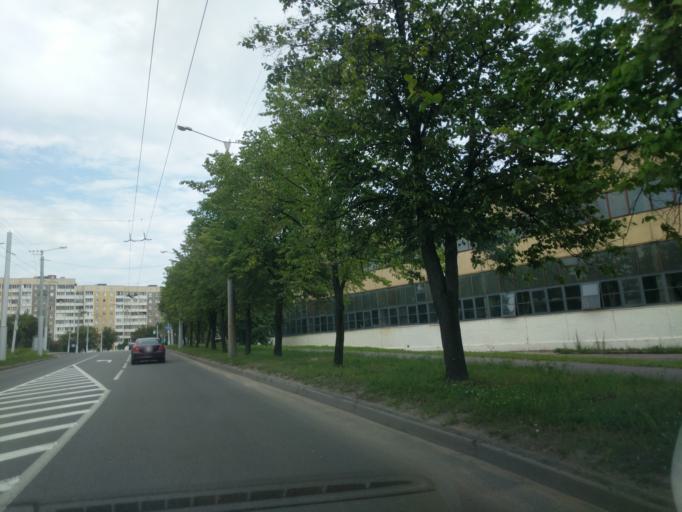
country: BY
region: Minsk
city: Novoye Medvezhino
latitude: 53.8921
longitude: 27.4841
